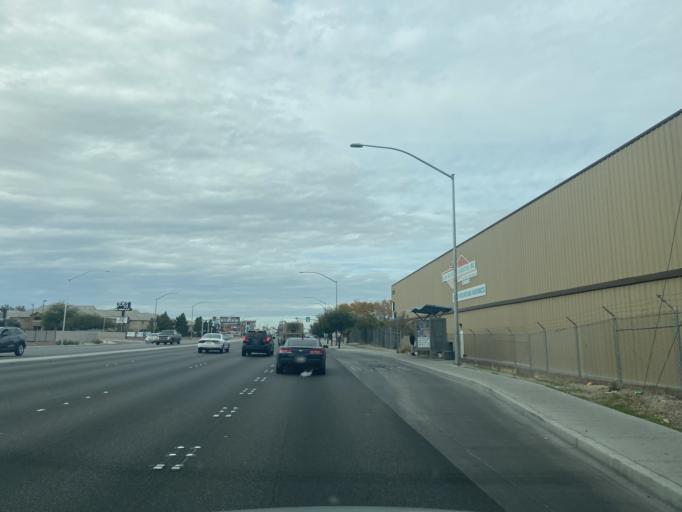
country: US
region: Nevada
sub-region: Clark County
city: Las Vegas
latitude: 36.2102
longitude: -115.2056
